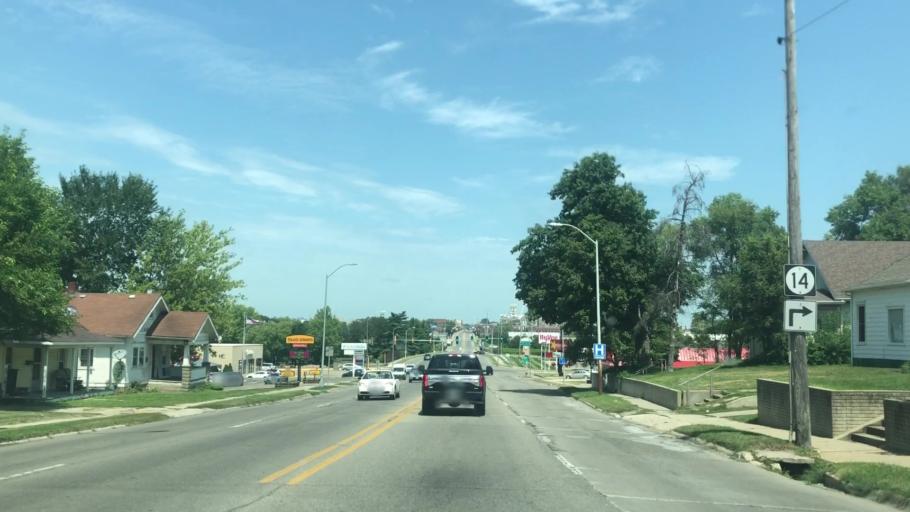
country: US
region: Iowa
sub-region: Marshall County
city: Marshalltown
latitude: 42.0364
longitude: -92.9127
